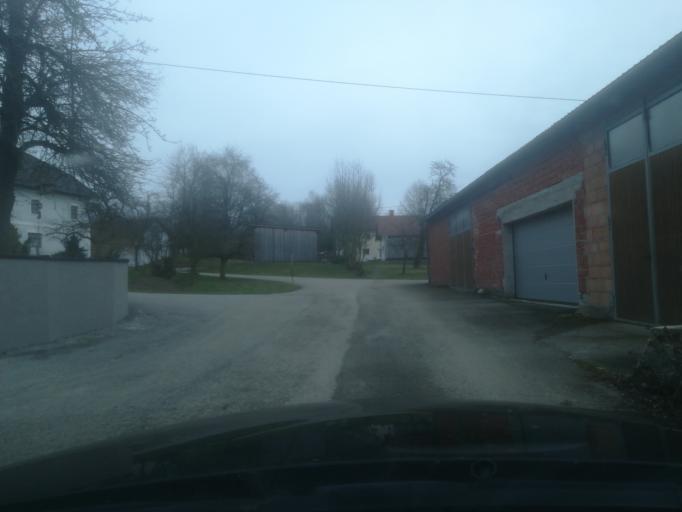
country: AT
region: Upper Austria
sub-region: Wels-Land
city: Neukirchen bei Lambach
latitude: 48.1054
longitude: 13.8241
